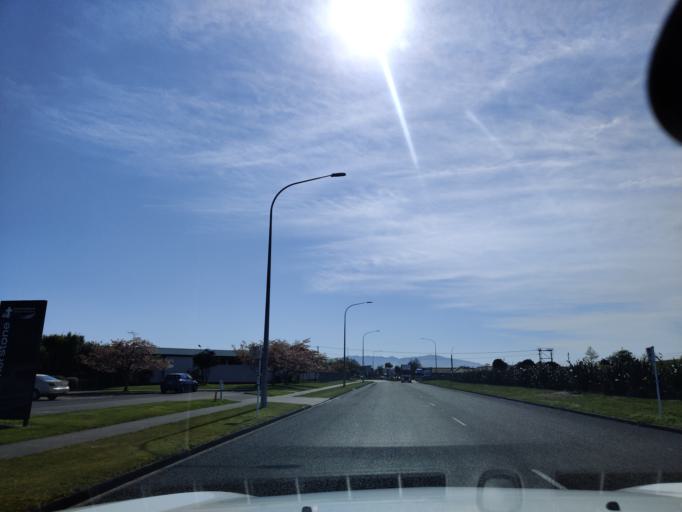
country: NZ
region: Manawatu-Wanganui
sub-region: Palmerston North City
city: Palmerston North
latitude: -40.3314
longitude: 175.6504
